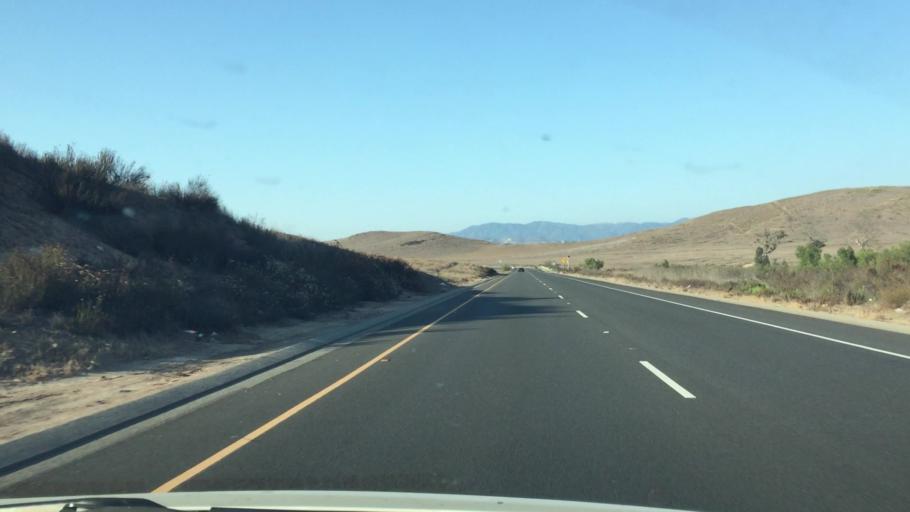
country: US
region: California
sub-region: Orange County
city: Laguna Woods
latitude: 33.6163
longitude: -117.7590
